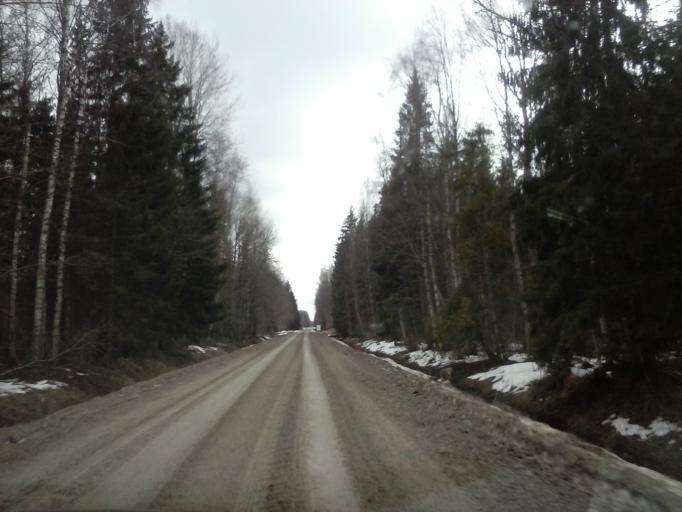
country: EE
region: Jogevamaa
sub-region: Mustvee linn
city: Mustvee
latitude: 59.0772
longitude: 26.8098
